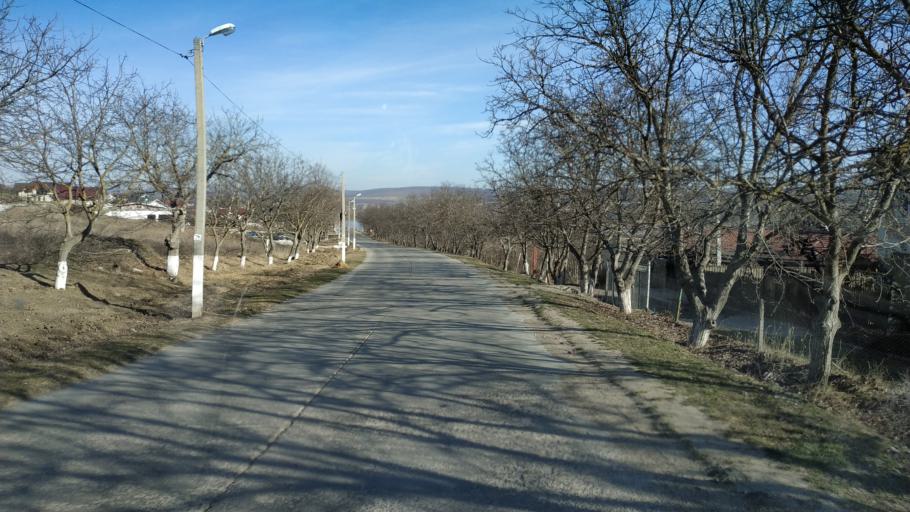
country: MD
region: Chisinau
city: Vatra
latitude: 46.9958
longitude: 28.6742
